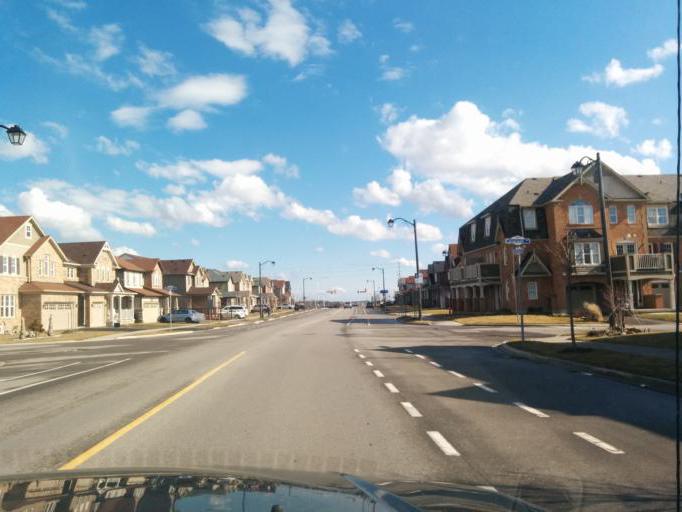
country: CA
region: Ontario
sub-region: Halton
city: Milton
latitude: 43.4929
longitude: -79.8558
